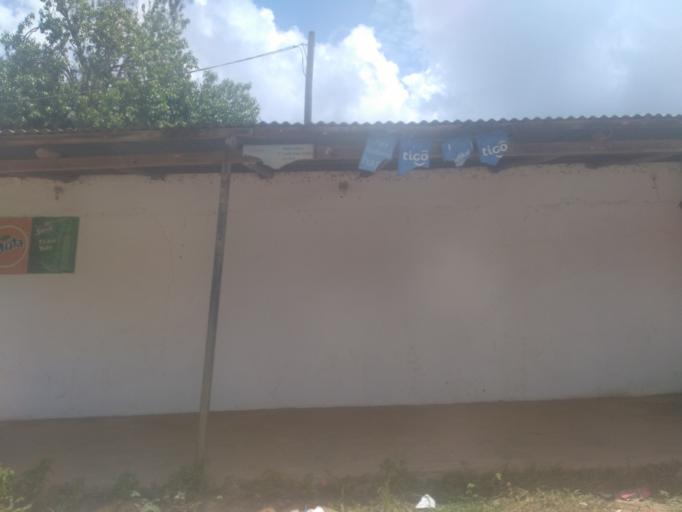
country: TZ
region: Zanzibar Urban/West
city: Zanzibar
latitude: -6.2169
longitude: 39.2124
